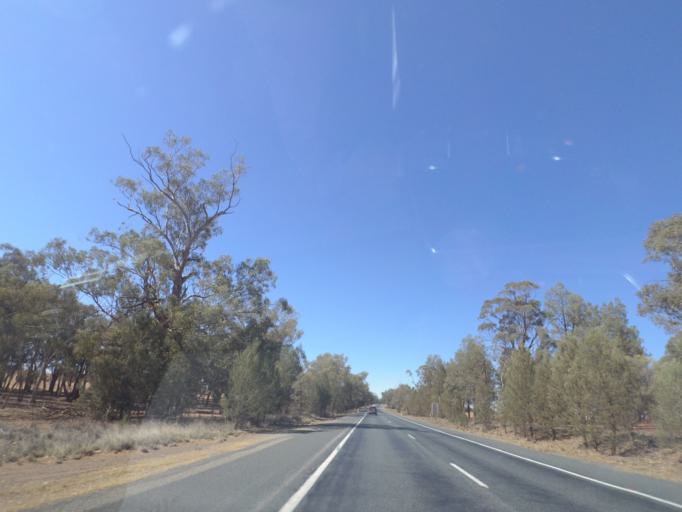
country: AU
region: New South Wales
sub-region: Bland
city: West Wyalong
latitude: -34.2016
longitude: 147.1102
